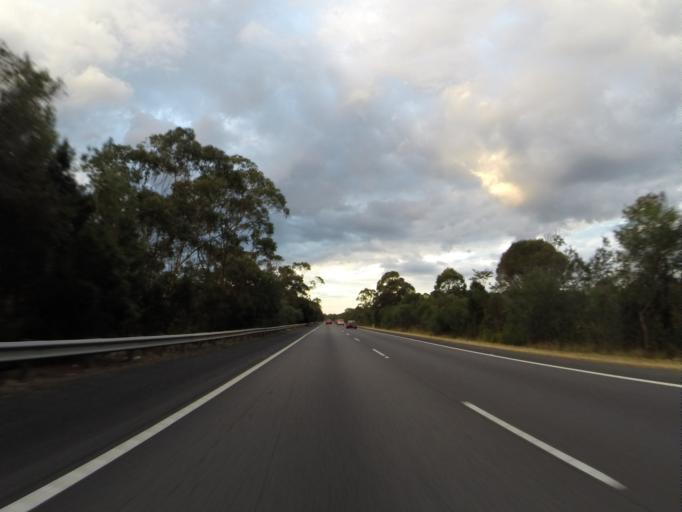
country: AU
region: New South Wales
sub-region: Wollondilly
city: Douglas Park
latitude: -34.2066
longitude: 150.6957
